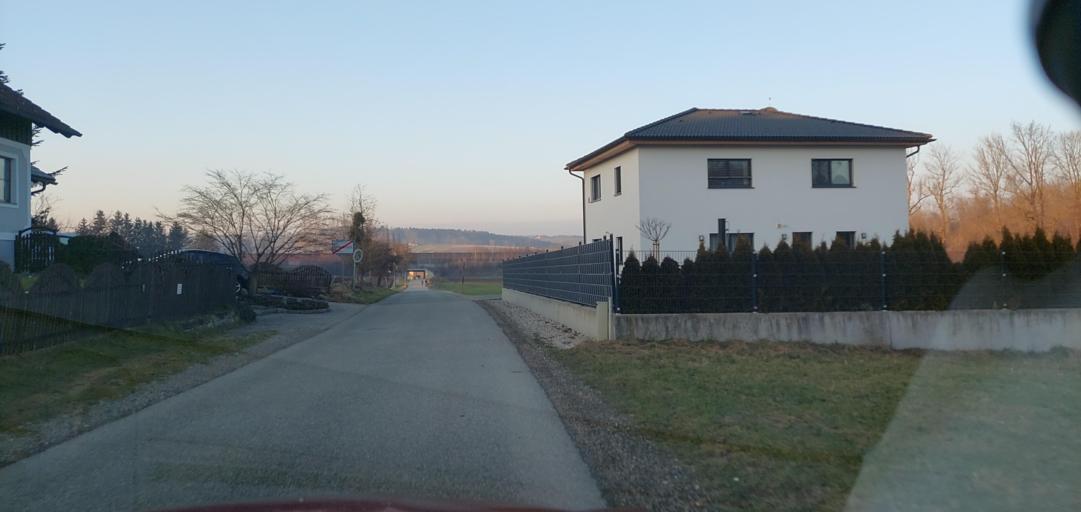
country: AT
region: Upper Austria
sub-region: Politischer Bezirk Grieskirchen
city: Bad Schallerbach
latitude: 48.1837
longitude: 13.9160
